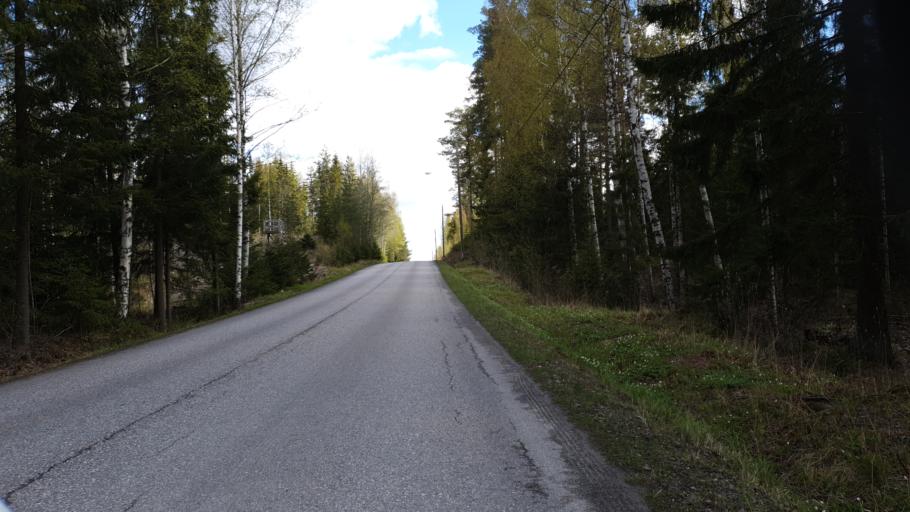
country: FI
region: Uusimaa
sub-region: Helsinki
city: Nurmijaervi
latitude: 60.3847
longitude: 24.8958
